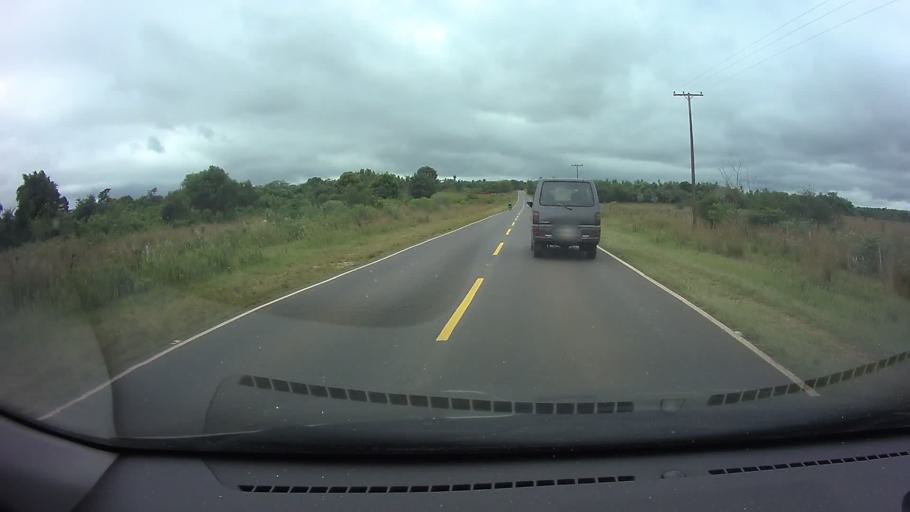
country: PY
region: Paraguari
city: Yaguaron
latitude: -25.7148
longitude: -57.3362
